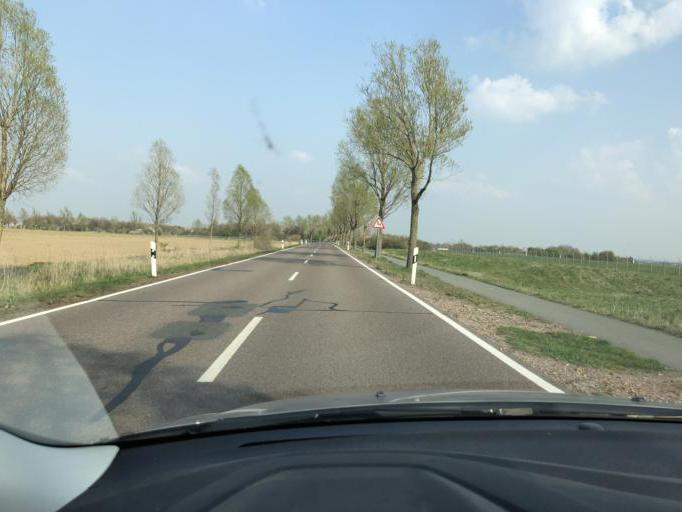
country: DE
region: Saxony
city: Zwochau
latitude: 51.4367
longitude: 12.2660
